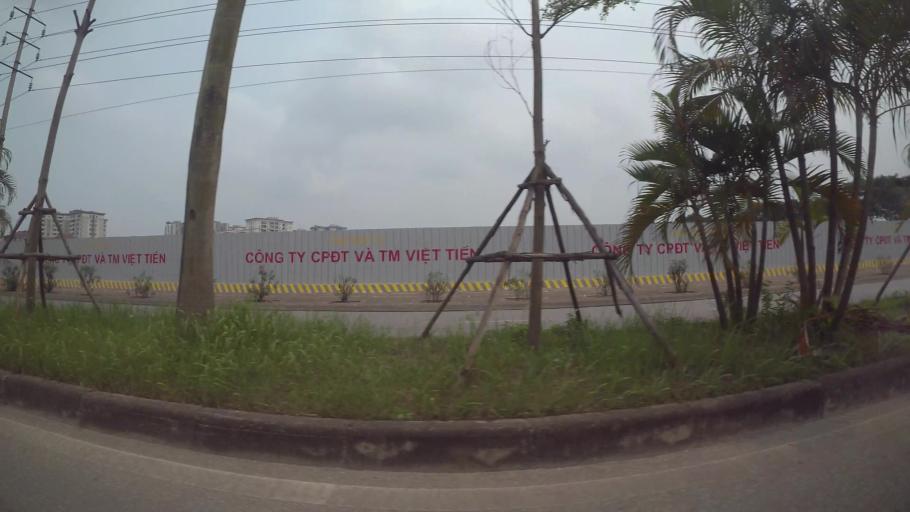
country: VN
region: Ha Noi
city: Trau Quy
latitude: 21.0649
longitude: 105.9052
